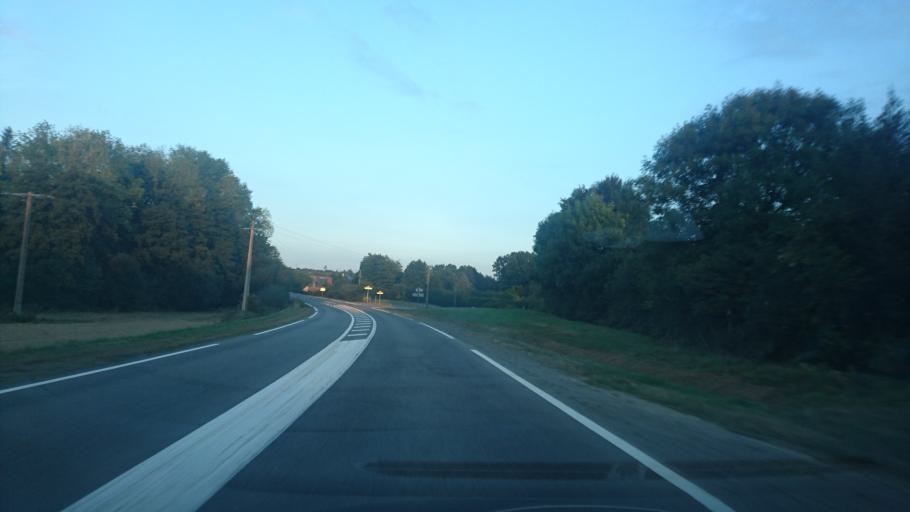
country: FR
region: Brittany
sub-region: Departement d'Ille-et-Vilaine
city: Maure-de-Bretagne
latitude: 47.9237
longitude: -1.9507
